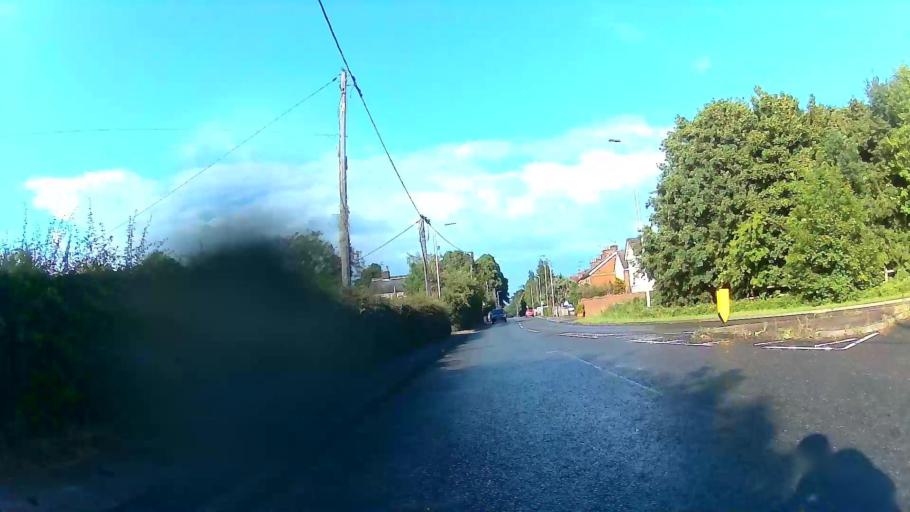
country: GB
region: England
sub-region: Essex
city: Writtle
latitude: 51.7285
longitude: 0.4101
